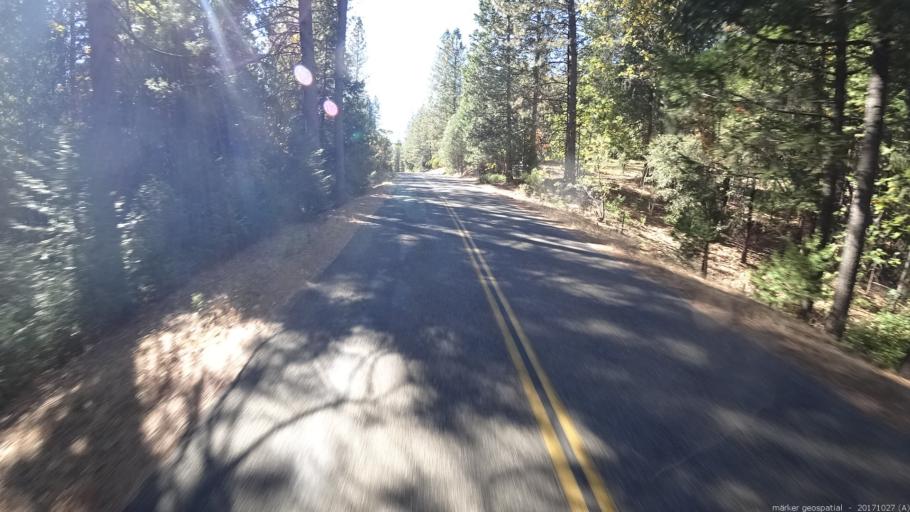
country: US
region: California
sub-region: Shasta County
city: Shingletown
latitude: 40.6894
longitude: -121.9255
